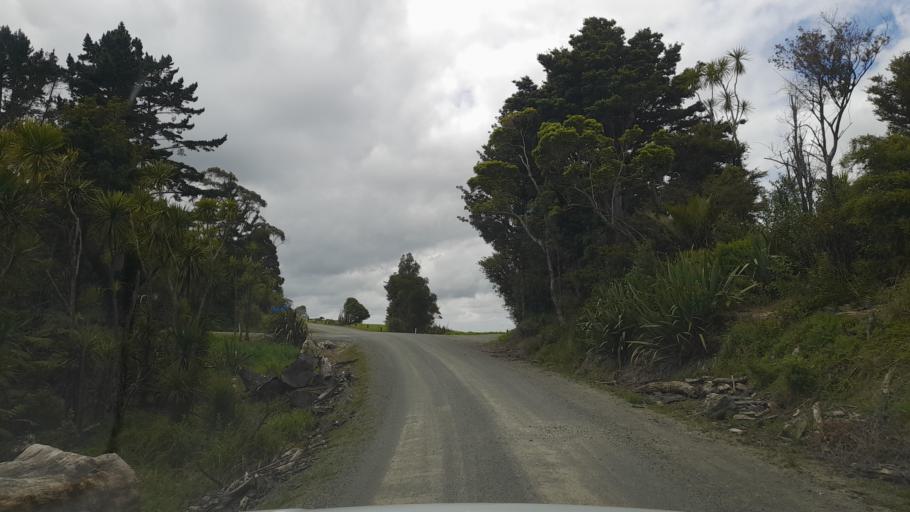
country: NZ
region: Auckland
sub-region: Auckland
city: Wellsford
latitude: -36.1810
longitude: 174.3448
